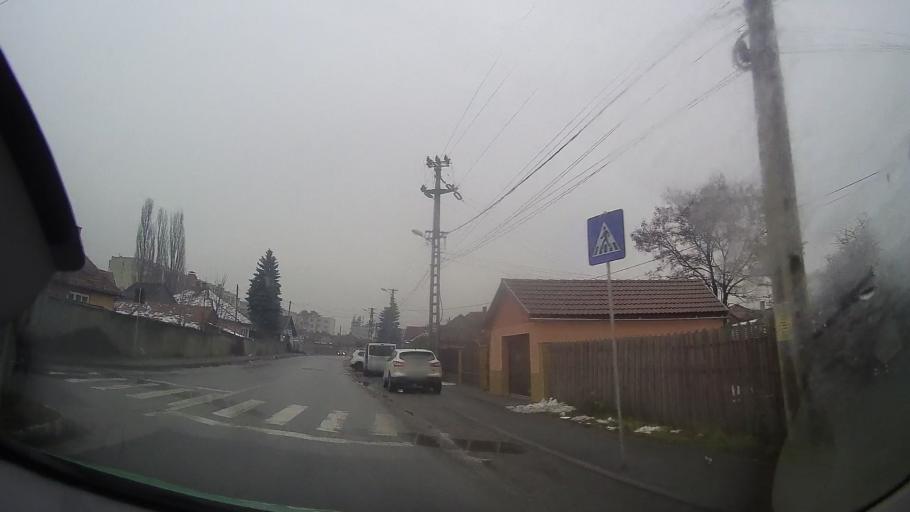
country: RO
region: Harghita
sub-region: Municipiul Gheorgheni
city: Gheorgheni
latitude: 46.7242
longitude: 25.5891
